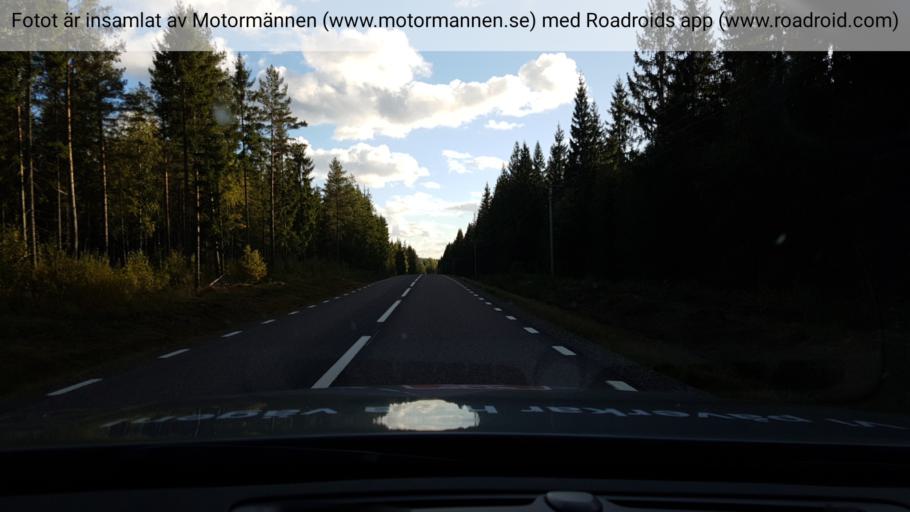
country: SE
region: Vaermland
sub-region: Karlstads Kommun
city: Molkom
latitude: 59.7631
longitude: 13.6979
